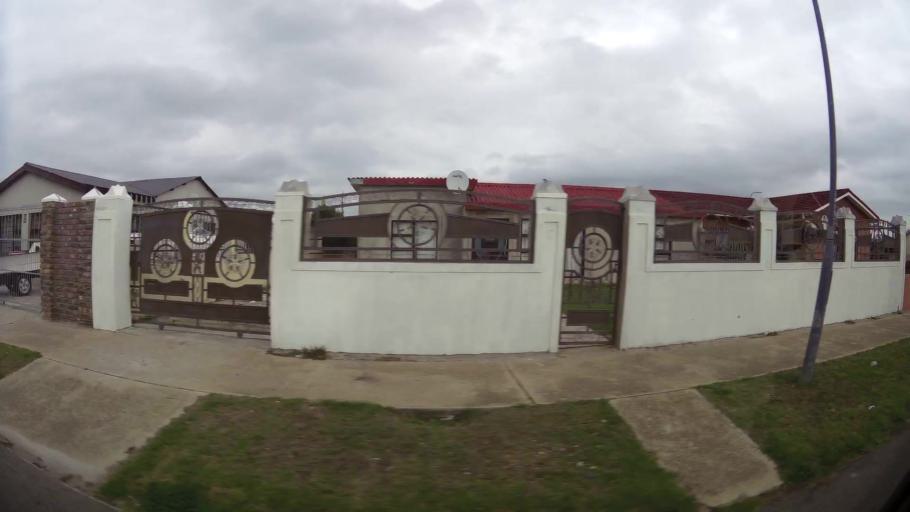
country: ZA
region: Eastern Cape
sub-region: Nelson Mandela Bay Metropolitan Municipality
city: Port Elizabeth
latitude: -33.8995
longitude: 25.5620
